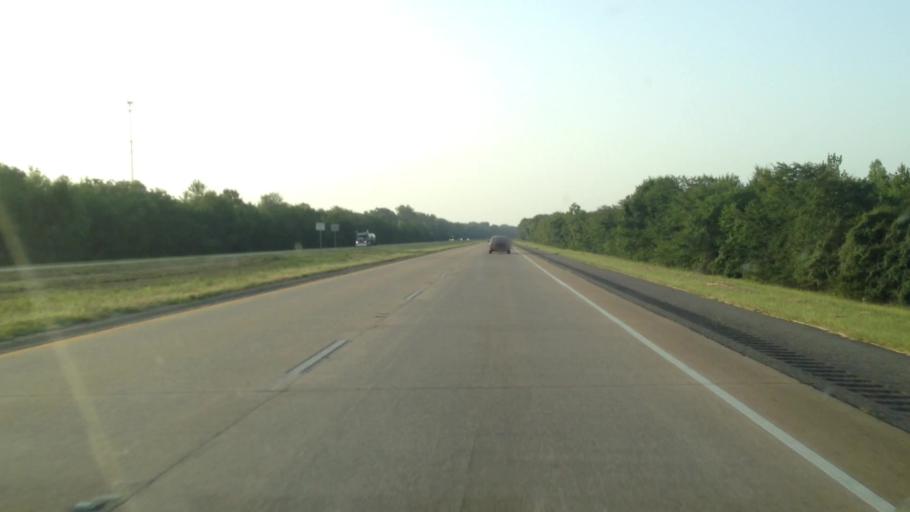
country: US
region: Louisiana
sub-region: Natchitoches Parish
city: Vienna Bend
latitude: 31.5537
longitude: -92.9739
